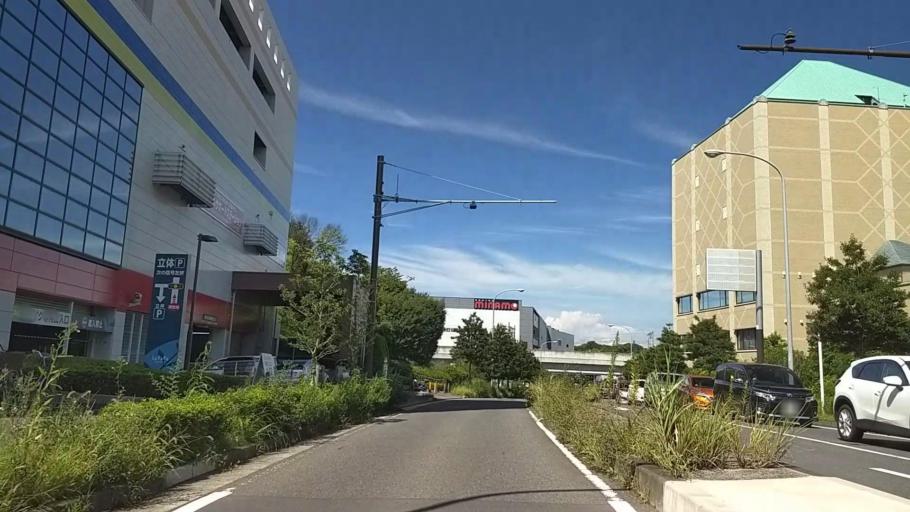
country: JP
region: Tokyo
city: Chofugaoka
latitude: 35.5495
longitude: 139.5784
